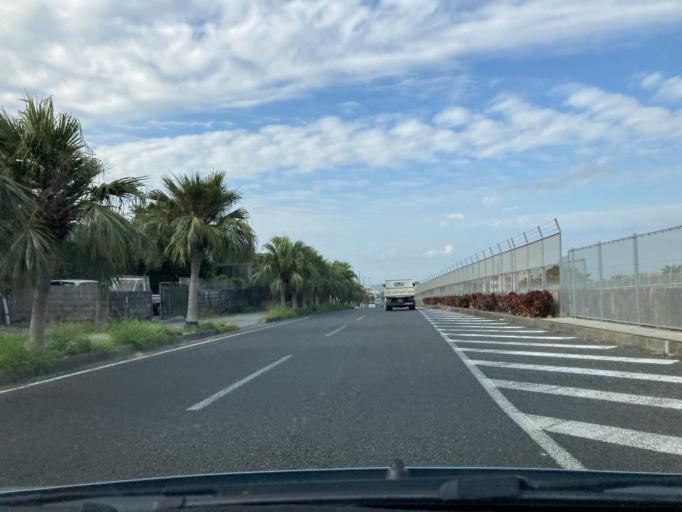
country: JP
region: Okinawa
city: Okinawa
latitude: 26.3267
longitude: 127.7864
